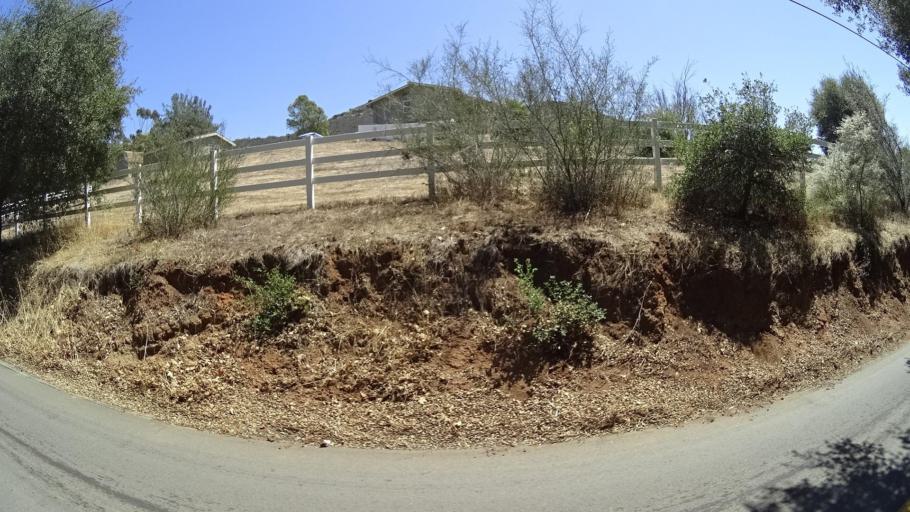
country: US
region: California
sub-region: San Diego County
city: Rainbow
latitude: 33.3812
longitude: -117.1417
